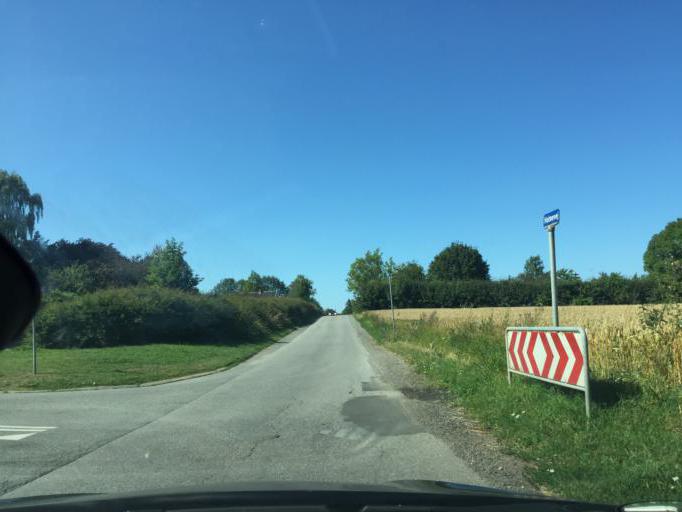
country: DK
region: South Denmark
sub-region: Nordfyns Kommune
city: Sonderso
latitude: 55.4798
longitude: 10.2666
